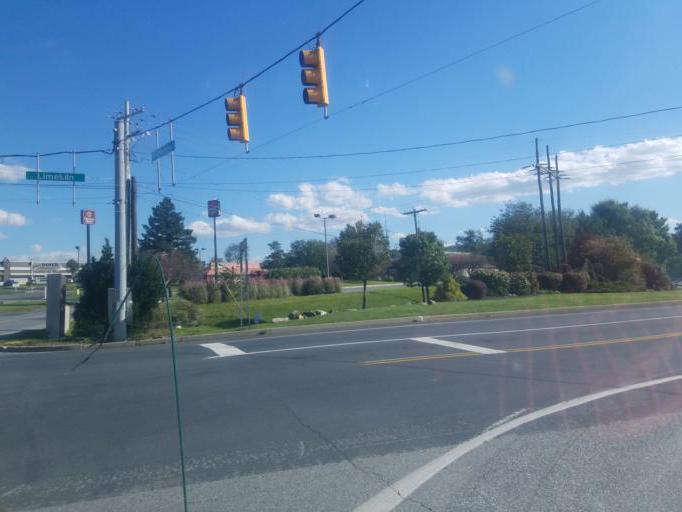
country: US
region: Pennsylvania
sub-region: Cumberland County
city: New Cumberland
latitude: 40.2138
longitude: -76.8790
